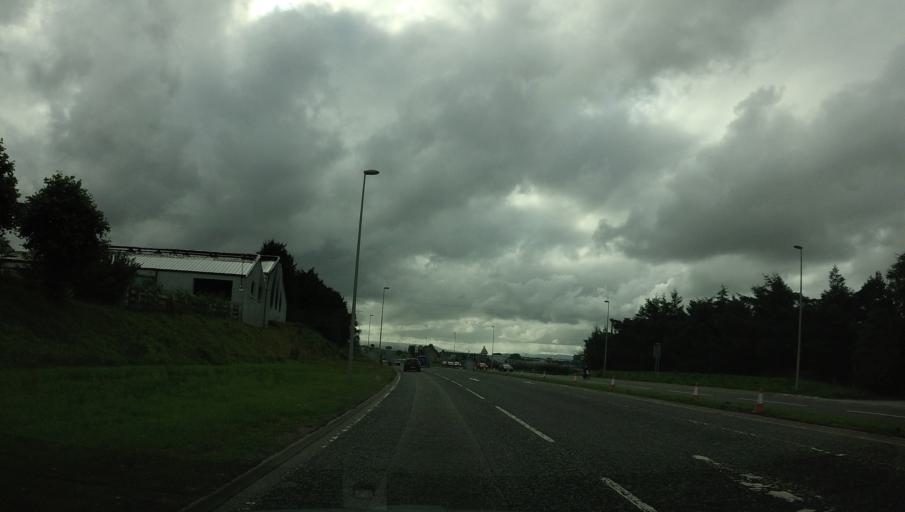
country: GB
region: Scotland
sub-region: Aberdeenshire
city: Westhill
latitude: 57.1477
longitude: -2.2473
